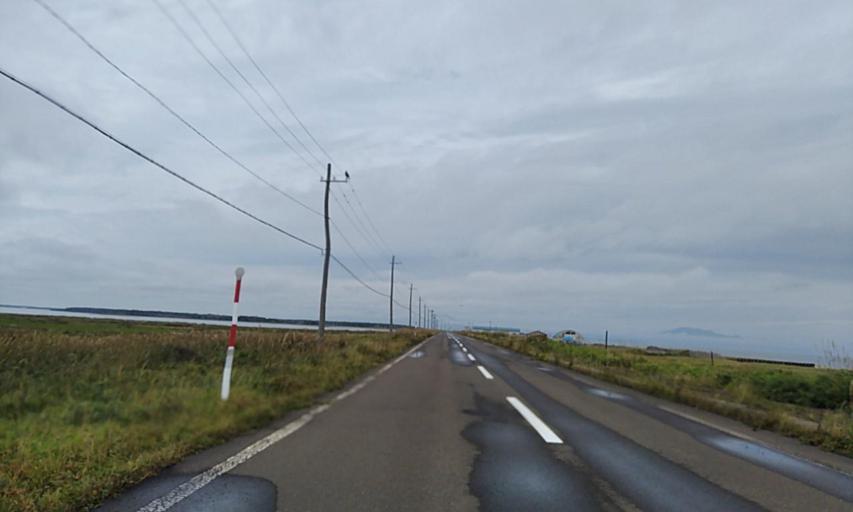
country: JP
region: Hokkaido
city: Shibetsu
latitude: 43.5972
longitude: 145.3210
